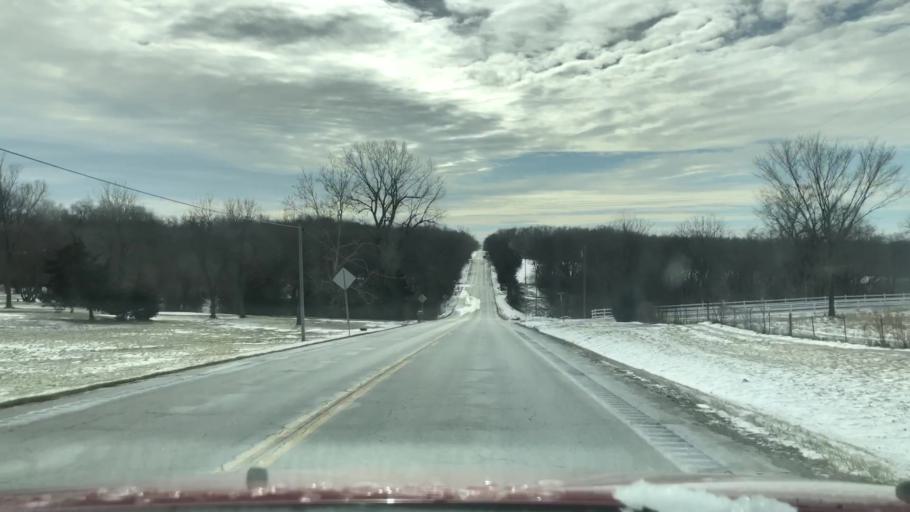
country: US
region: Missouri
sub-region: Jackson County
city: Lone Jack
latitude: 38.8904
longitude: -94.1345
